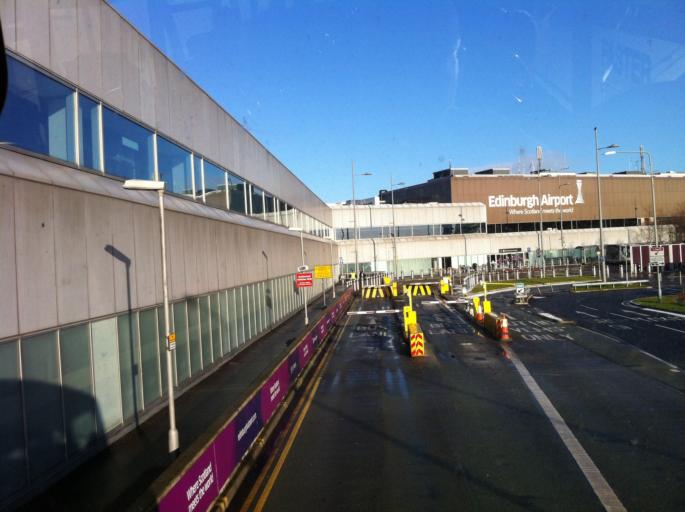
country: GB
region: Scotland
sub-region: Edinburgh
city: Ratho
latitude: 55.9471
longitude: -3.3650
